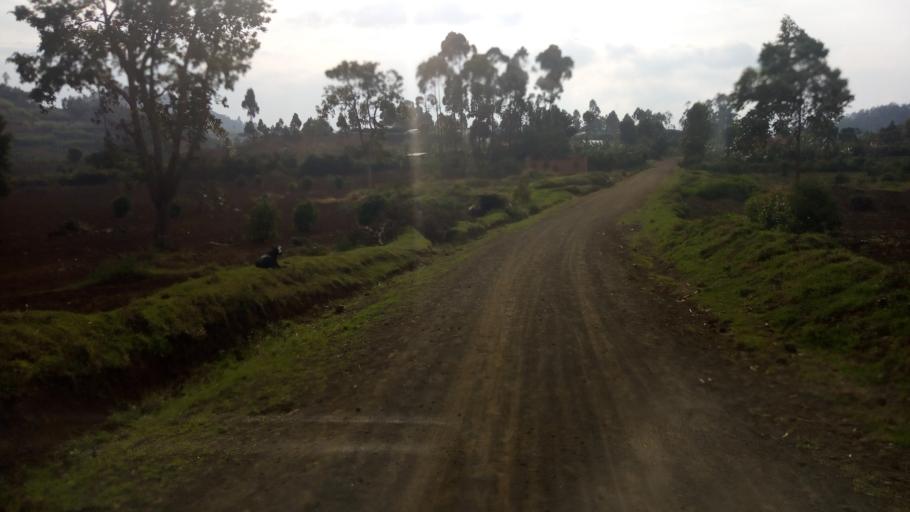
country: UG
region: Western Region
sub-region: Kisoro District
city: Kisoro
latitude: -1.3060
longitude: 29.7113
